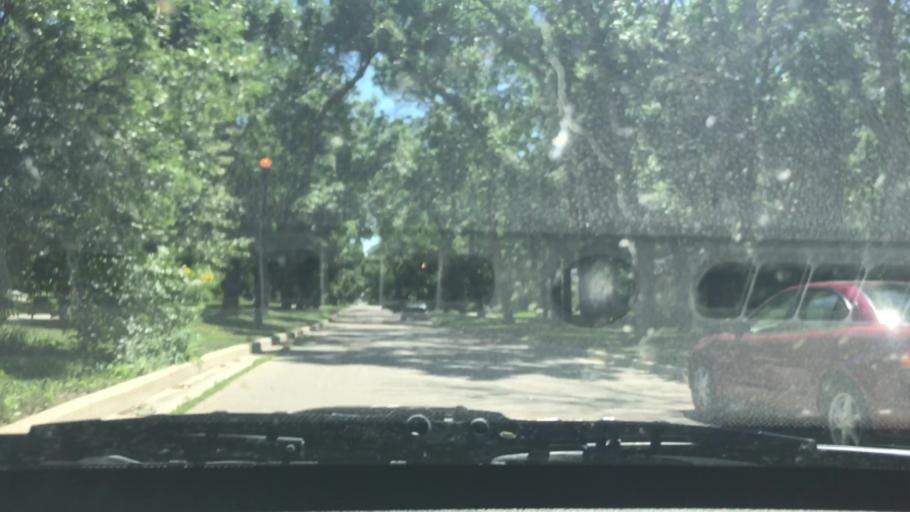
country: CA
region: Manitoba
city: Winnipeg
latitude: 49.8725
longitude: -97.1957
